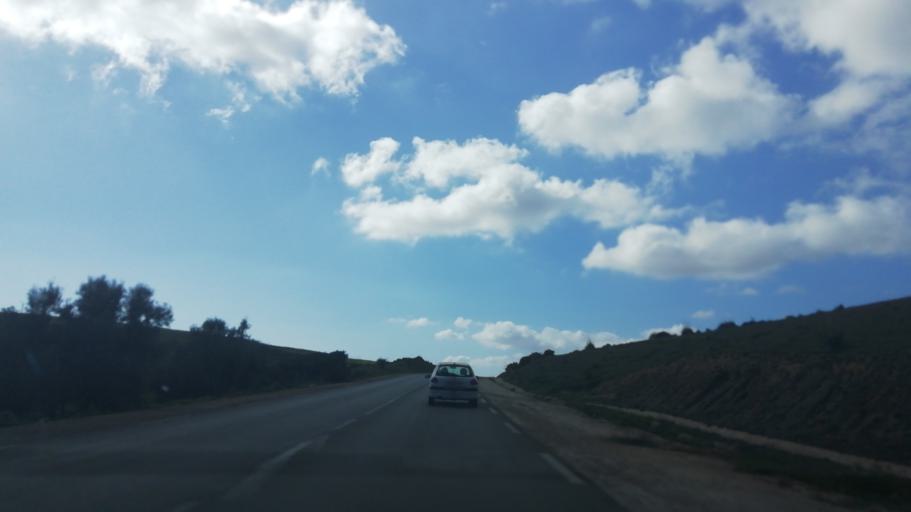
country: DZ
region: Relizane
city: Relizane
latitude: 36.0926
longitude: 0.4632
